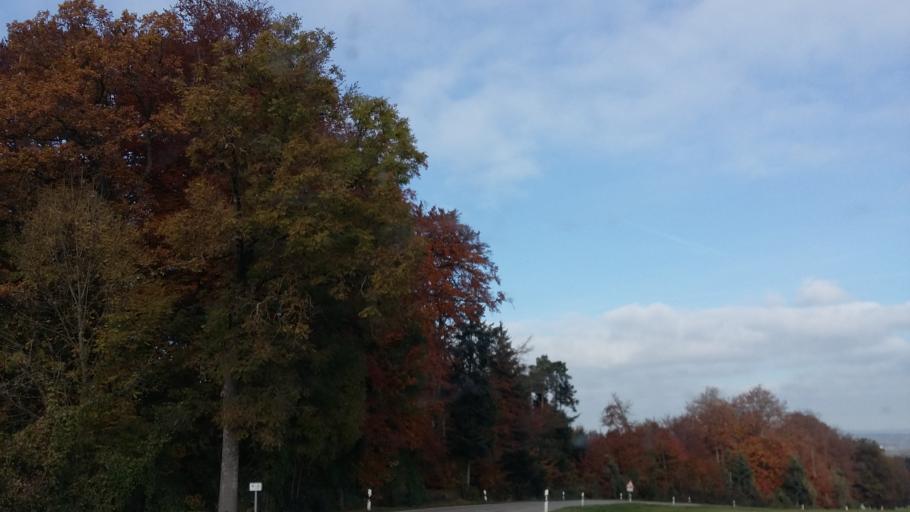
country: DE
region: Bavaria
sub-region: Upper Bavaria
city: Irschenberg
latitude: 47.8483
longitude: 11.9323
